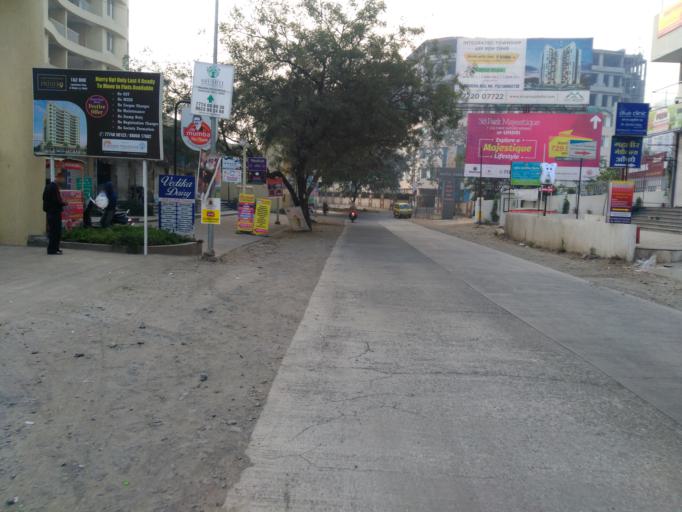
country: IN
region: Maharashtra
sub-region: Pune Division
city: Pune
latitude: 18.4550
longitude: 73.9138
